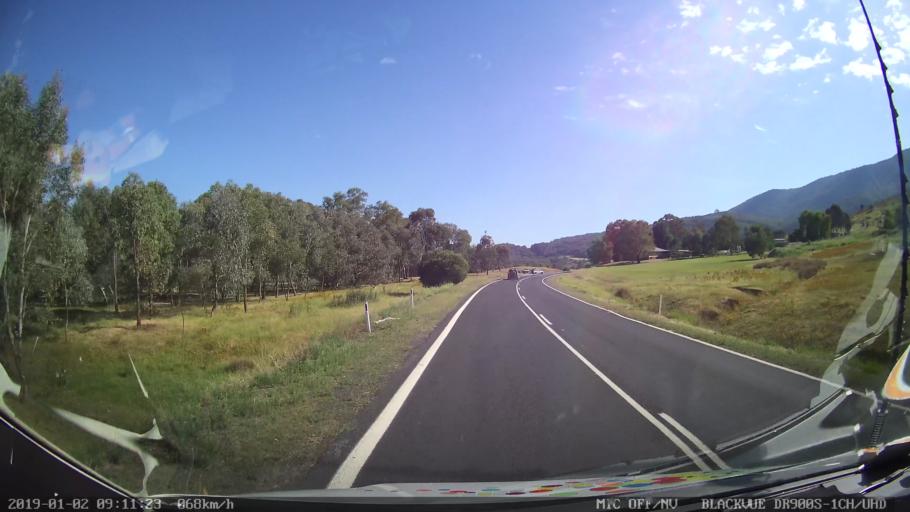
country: AU
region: New South Wales
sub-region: Tumut Shire
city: Tumut
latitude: -35.5117
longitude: 148.2688
